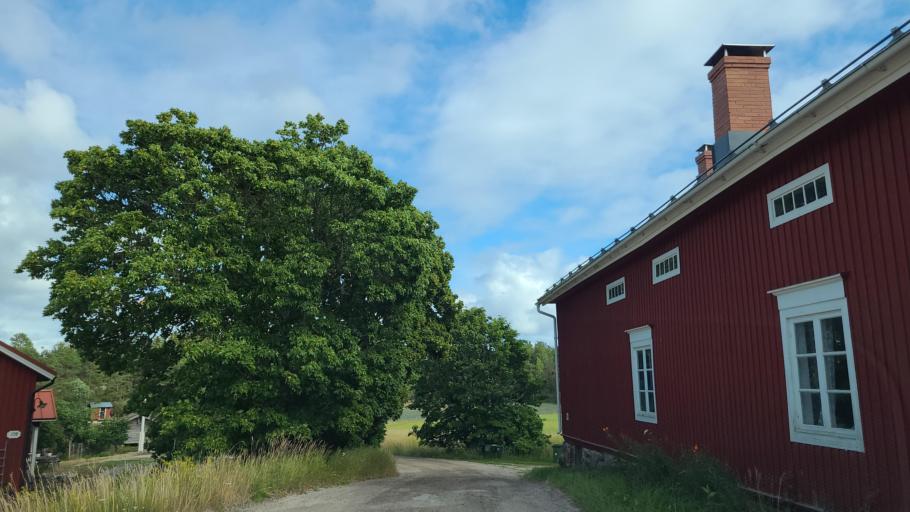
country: FI
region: Varsinais-Suomi
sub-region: Aboland-Turunmaa
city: Nagu
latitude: 60.1415
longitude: 21.7958
